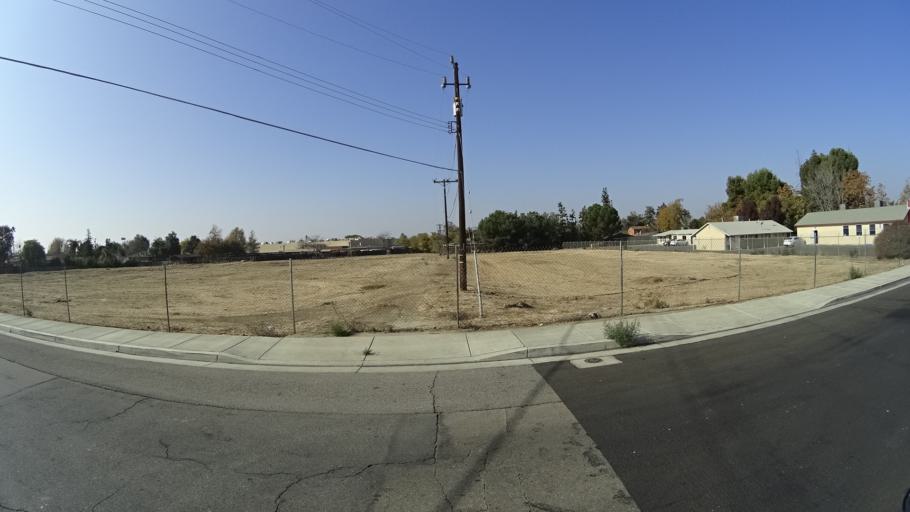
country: US
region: California
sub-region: Kern County
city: Bakersfield
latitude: 35.3430
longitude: -119.0343
